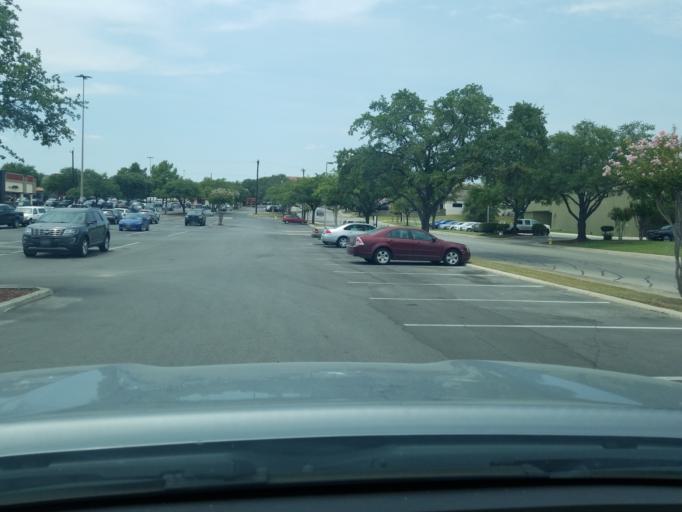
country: US
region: Texas
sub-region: Bexar County
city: Hollywood Park
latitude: 29.5639
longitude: -98.4874
